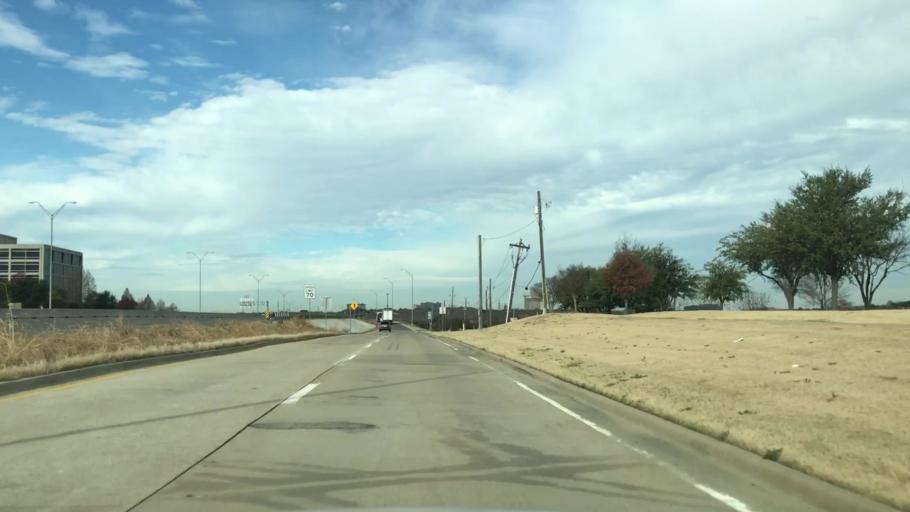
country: US
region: Texas
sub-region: Dallas County
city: Coppell
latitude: 32.8995
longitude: -96.9785
